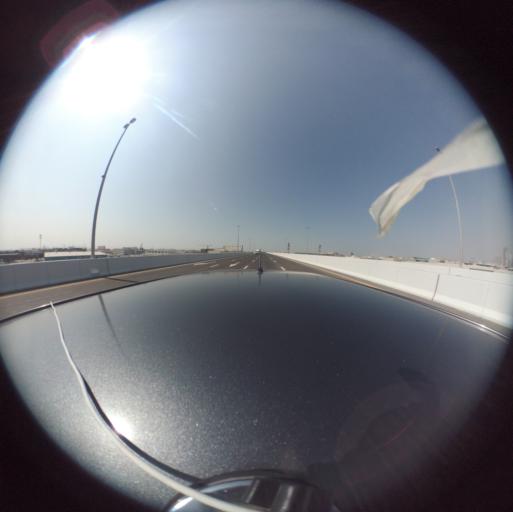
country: AE
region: Dubai
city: Dubai
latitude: 25.1564
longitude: 55.2342
